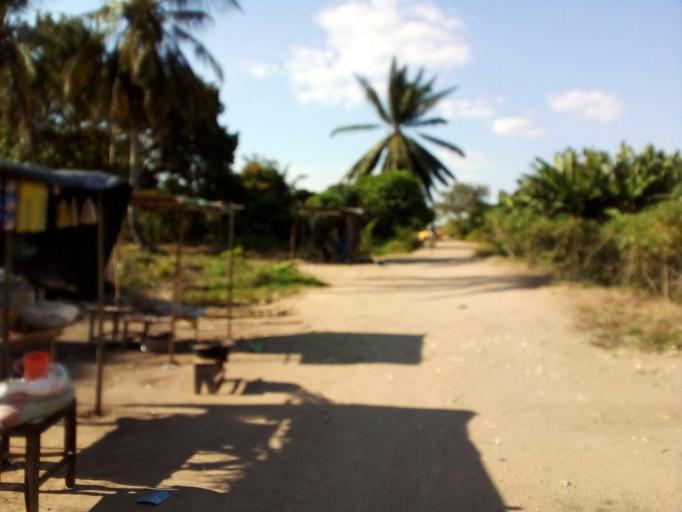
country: MZ
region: Zambezia
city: Quelimane
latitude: -17.5931
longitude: 36.8328
